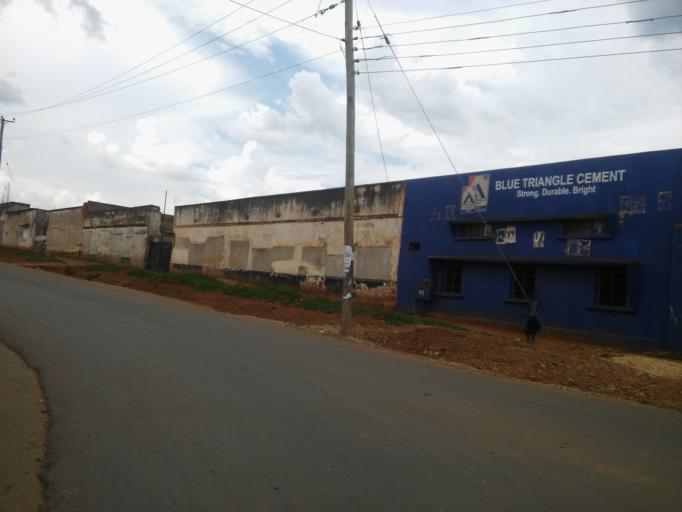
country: UG
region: Eastern Region
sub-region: Mbale District
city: Mbale
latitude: 1.0769
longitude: 34.1601
